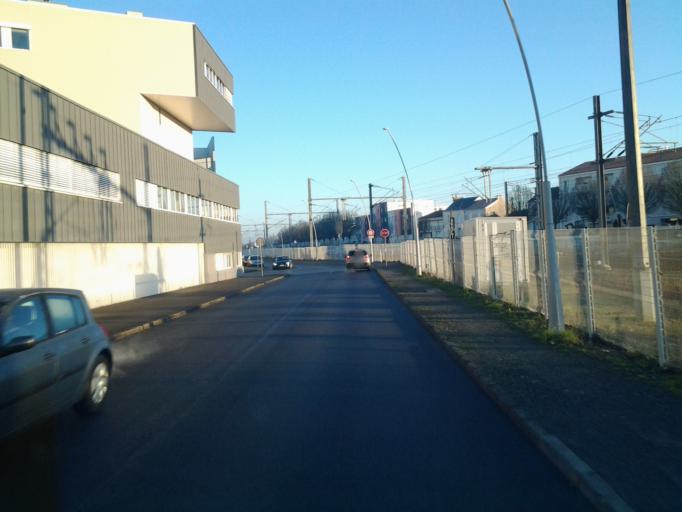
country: FR
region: Pays de la Loire
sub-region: Departement de la Vendee
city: La Roche-sur-Yon
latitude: 46.6766
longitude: -1.4366
